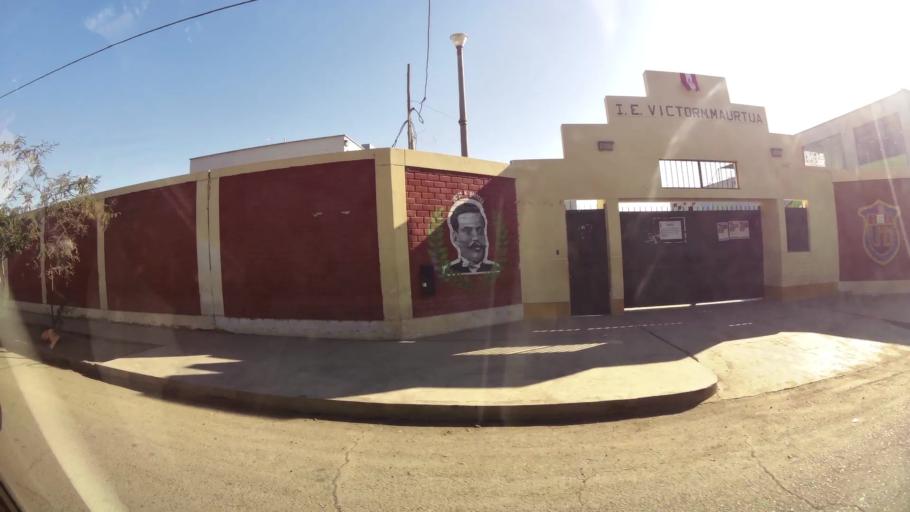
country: PE
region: Ica
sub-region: Provincia de Ica
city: La Tinguina
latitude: -14.0449
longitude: -75.7062
